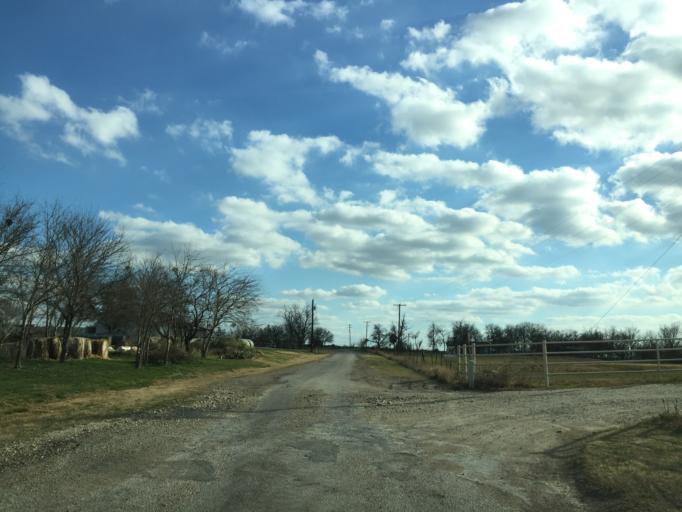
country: US
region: Texas
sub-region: Williamson County
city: Taylor
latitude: 30.6339
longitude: -97.4356
